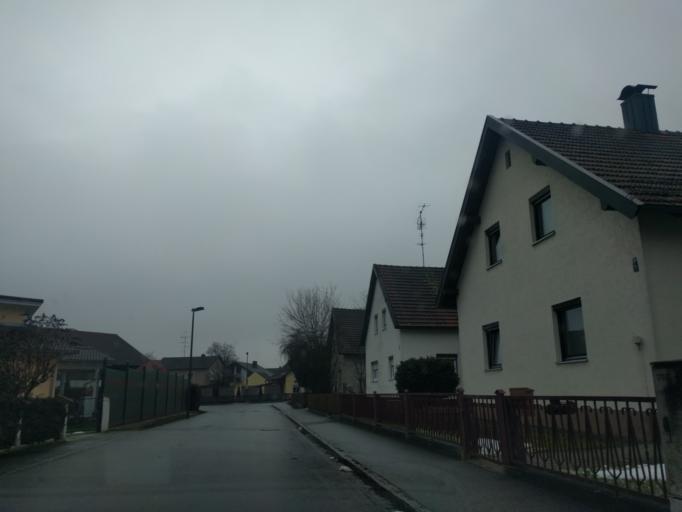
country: DE
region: Bavaria
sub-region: Lower Bavaria
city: Osterhofen
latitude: 48.7029
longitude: 13.0222
